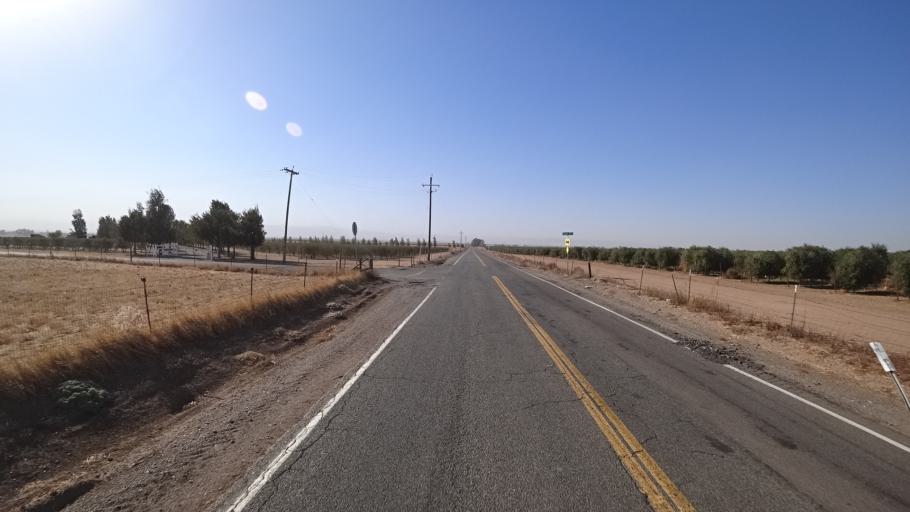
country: US
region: California
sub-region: Yolo County
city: Cottonwood
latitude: 38.7112
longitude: -121.8996
